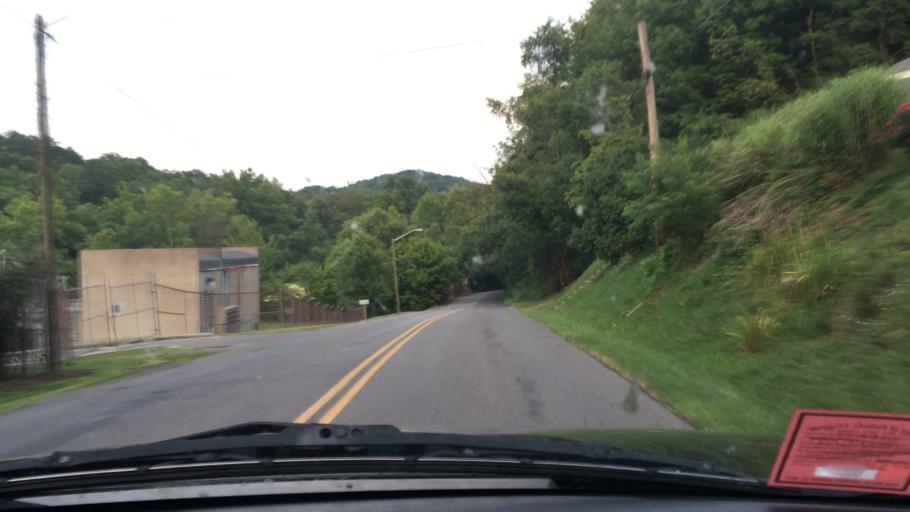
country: US
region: Virginia
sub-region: Pulaski County
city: Pulaski
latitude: 37.0427
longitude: -80.7491
